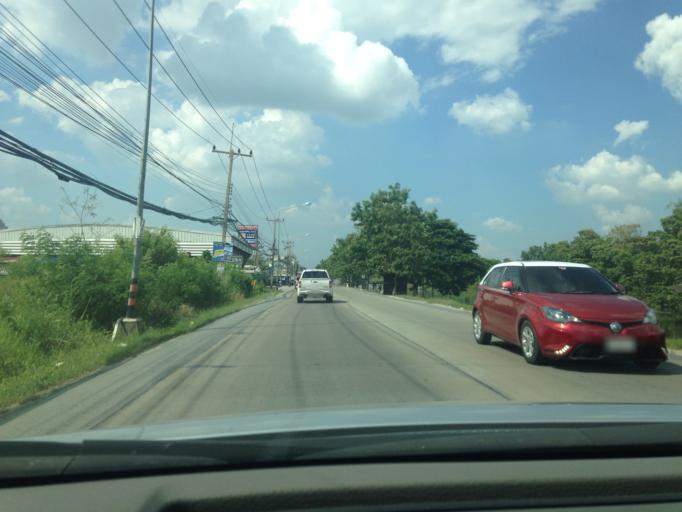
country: TH
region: Phra Nakhon Si Ayutthaya
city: Ban Bang Kadi Pathum Thani
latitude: 13.9867
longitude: 100.5994
